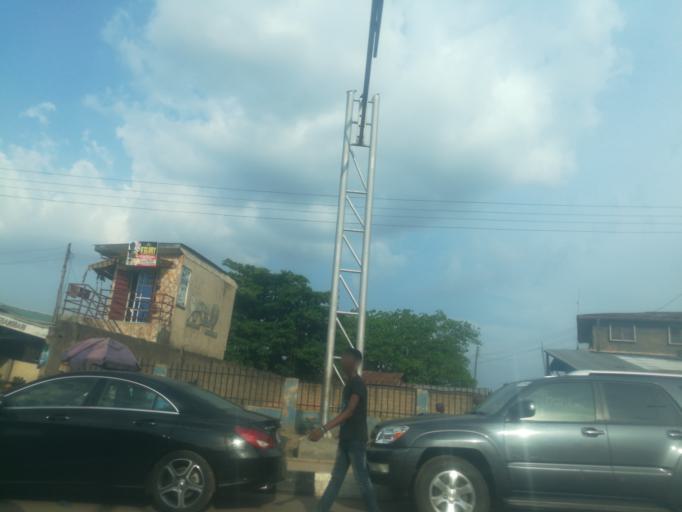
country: NG
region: Ogun
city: Abeokuta
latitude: 7.1470
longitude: 3.3299
